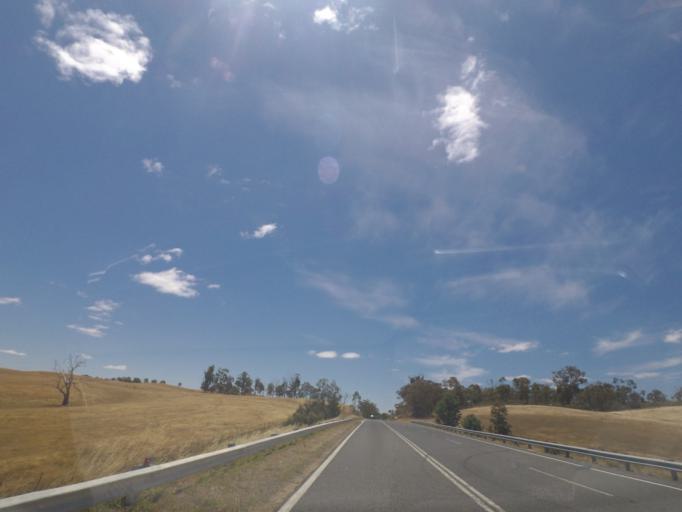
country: AU
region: Victoria
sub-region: Mount Alexander
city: Castlemaine
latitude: -37.2089
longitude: 144.1406
